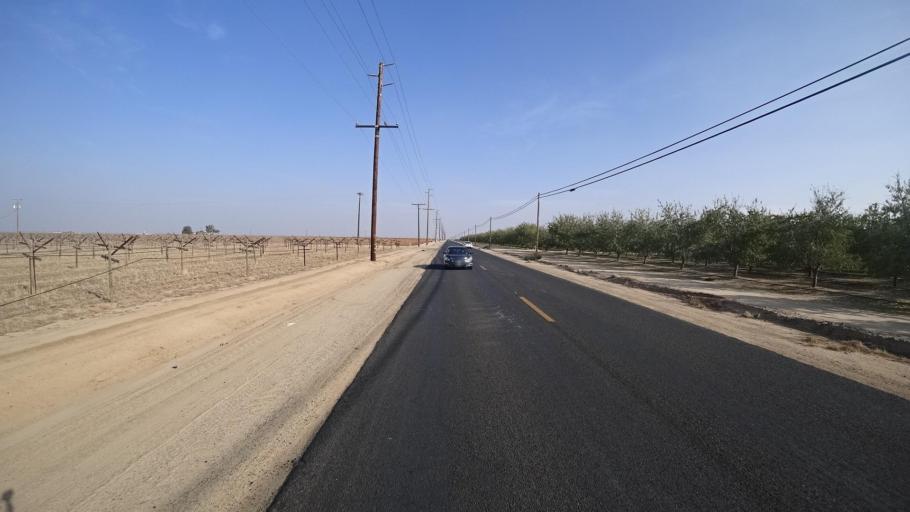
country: US
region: California
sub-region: Tulare County
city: Richgrove
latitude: 35.7761
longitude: -119.1391
